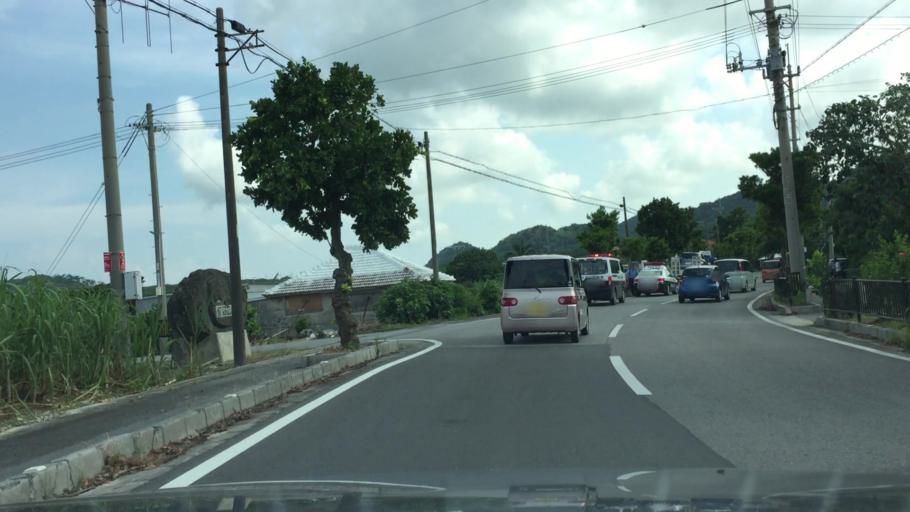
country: JP
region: Okinawa
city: Ishigaki
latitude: 24.4574
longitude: 124.2494
